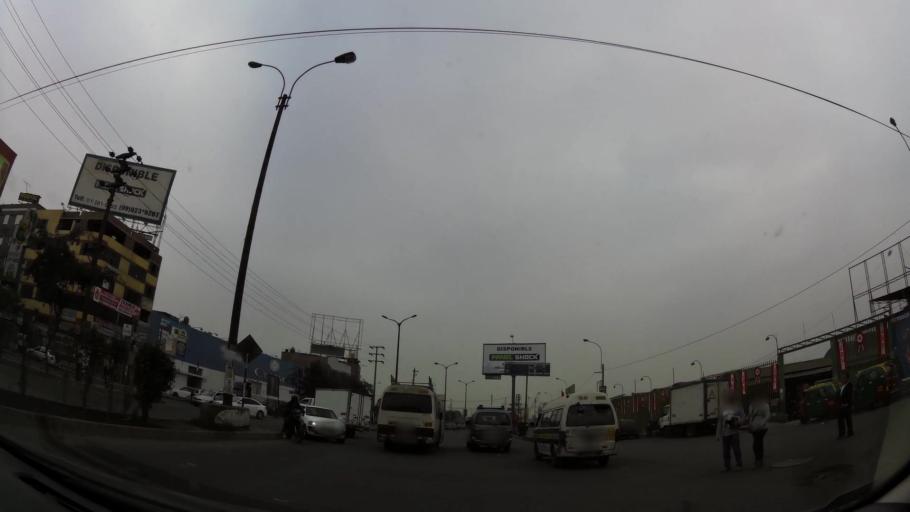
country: PE
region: Lima
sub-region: Lima
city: Vitarte
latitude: -12.0429
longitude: -76.9361
